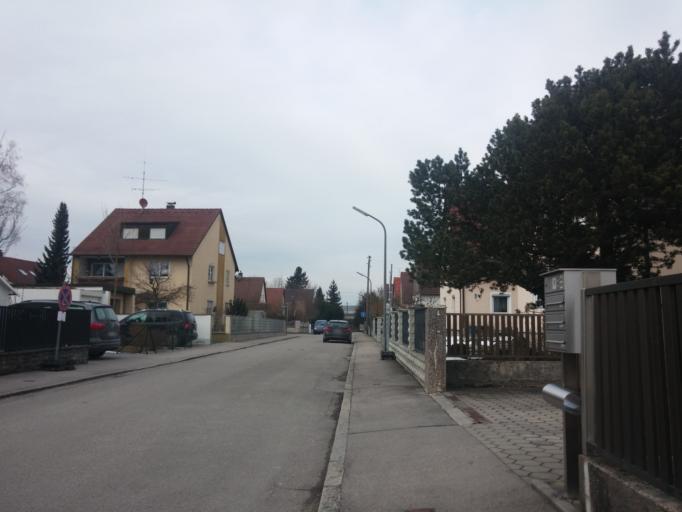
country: DE
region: Bavaria
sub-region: Upper Bavaria
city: Neubiberg
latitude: 48.1205
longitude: 11.6792
